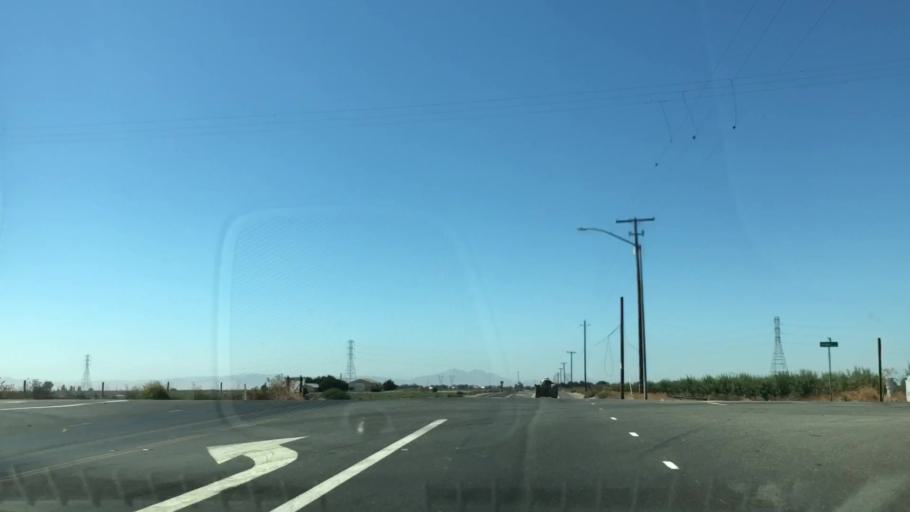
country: US
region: California
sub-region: San Joaquin County
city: Country Club
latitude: 37.9269
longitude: -121.3968
